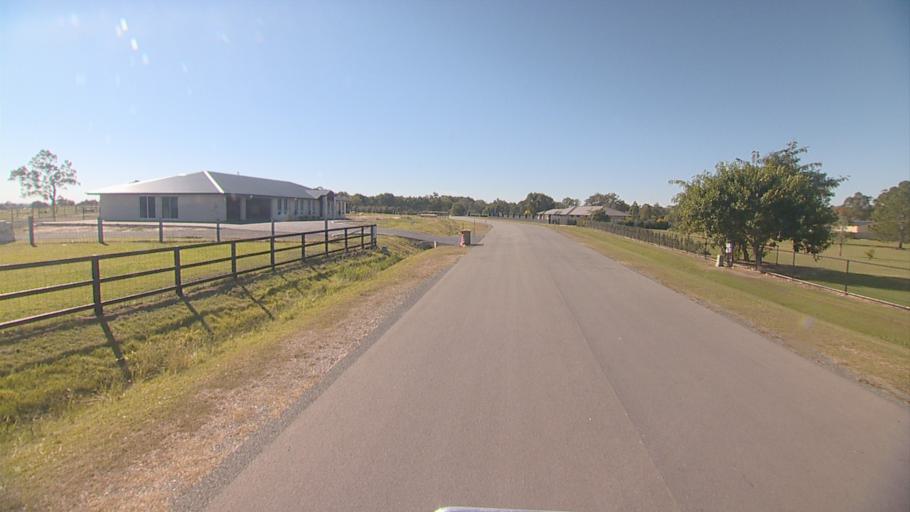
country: AU
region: Queensland
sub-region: Logan
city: Logan Reserve
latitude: -27.7266
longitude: 153.1230
